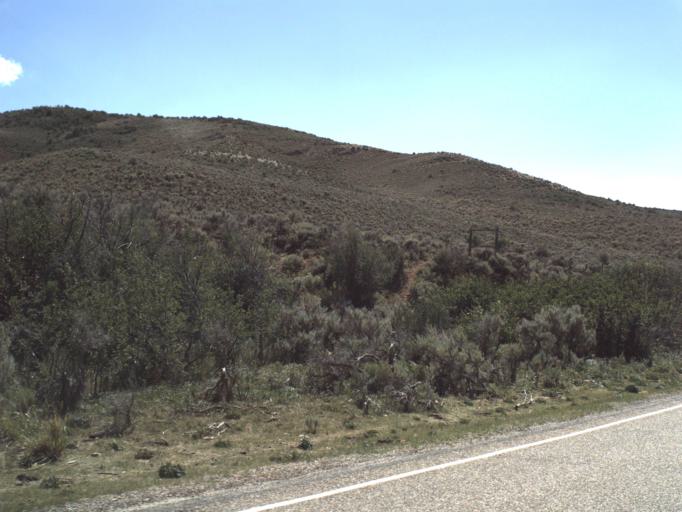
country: US
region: Utah
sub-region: Rich County
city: Randolph
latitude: 41.5040
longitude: -111.2968
